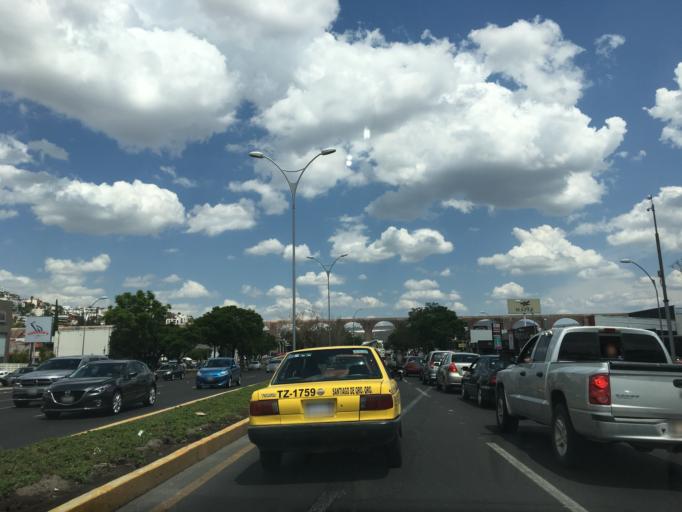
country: MX
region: Queretaro
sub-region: Queretaro
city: Santiago de Queretaro
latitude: 20.5986
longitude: -100.3744
